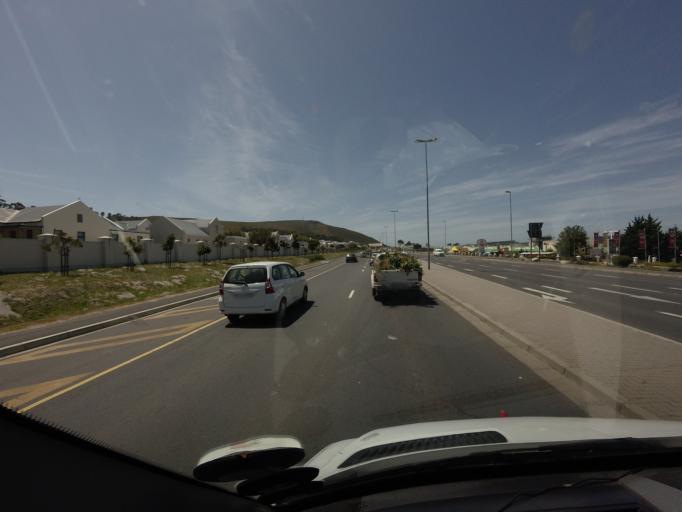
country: ZA
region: Western Cape
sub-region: Overberg District Municipality
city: Hermanus
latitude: -34.4127
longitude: 19.2028
